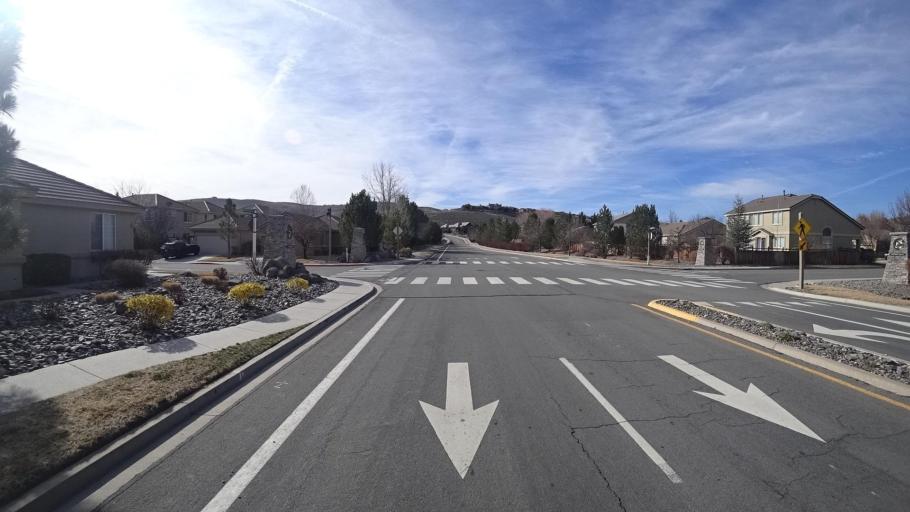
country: US
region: Nevada
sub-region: Washoe County
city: Spanish Springs
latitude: 39.6056
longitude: -119.6964
